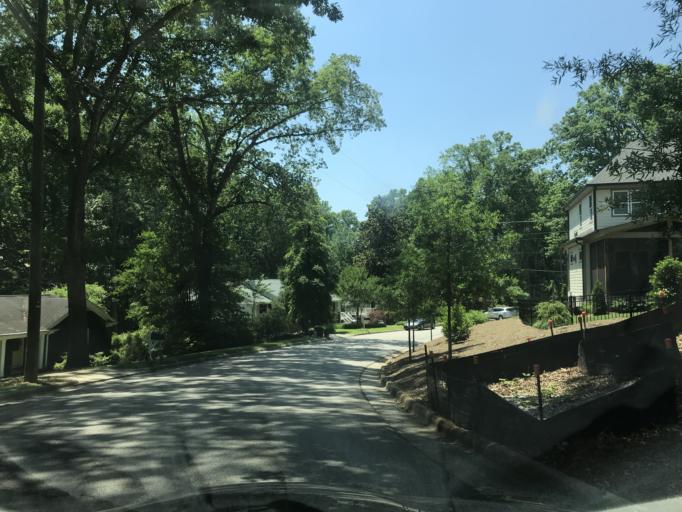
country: US
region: North Carolina
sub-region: Wake County
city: West Raleigh
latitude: 35.8392
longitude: -78.6496
